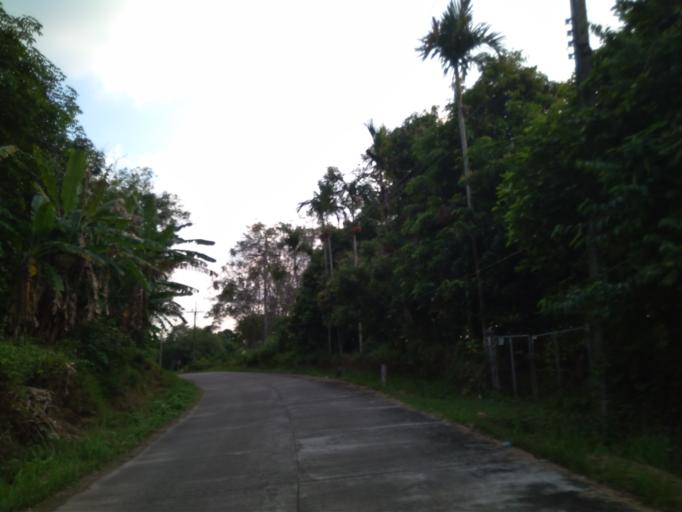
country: TH
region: Phangnga
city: Ko Yao
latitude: 8.1454
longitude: 98.5983
